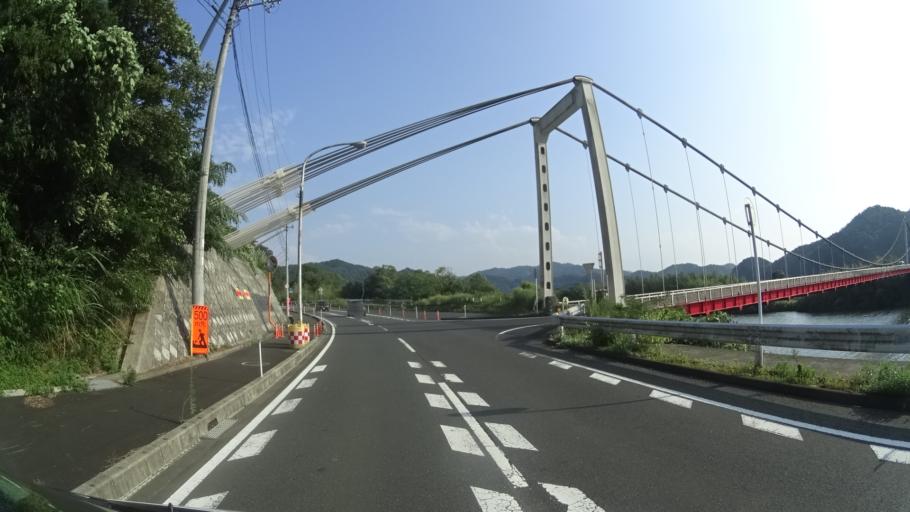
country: JP
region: Kyoto
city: Maizuru
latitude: 35.4672
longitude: 135.2833
